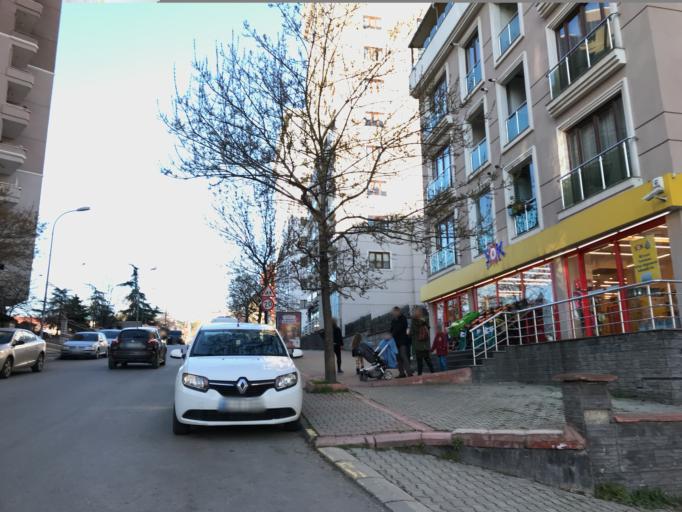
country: TR
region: Istanbul
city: Maltepe
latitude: 40.9411
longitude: 29.1406
